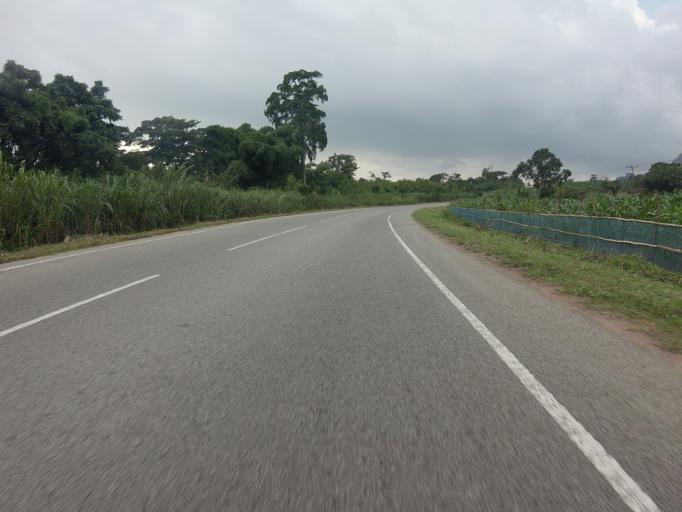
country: GH
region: Volta
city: Ho
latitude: 6.7606
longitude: 0.4795
